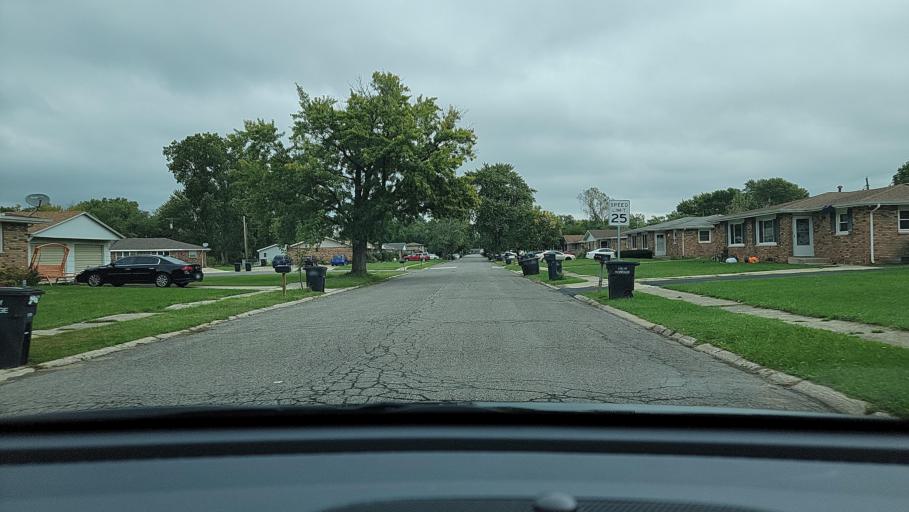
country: US
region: Indiana
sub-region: Porter County
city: Portage
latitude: 41.5557
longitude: -87.2030
